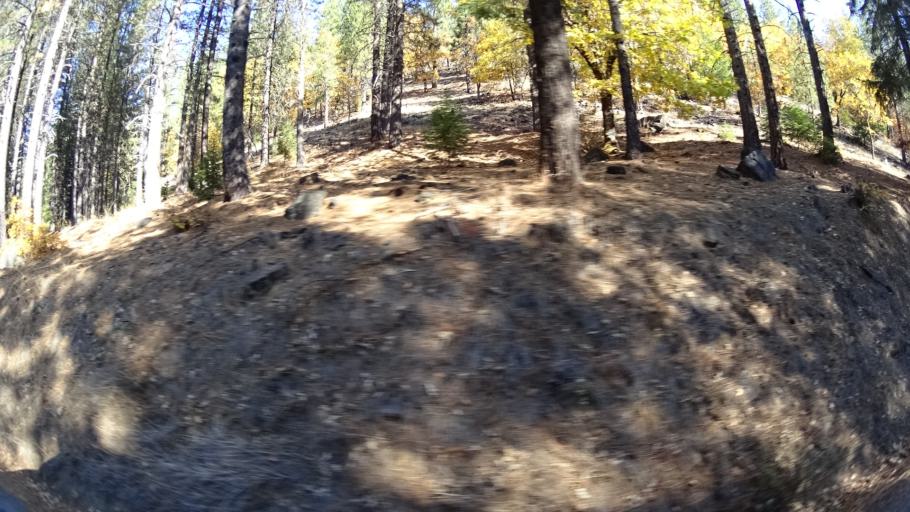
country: US
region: California
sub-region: Siskiyou County
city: Yreka
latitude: 41.6403
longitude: -123.0116
